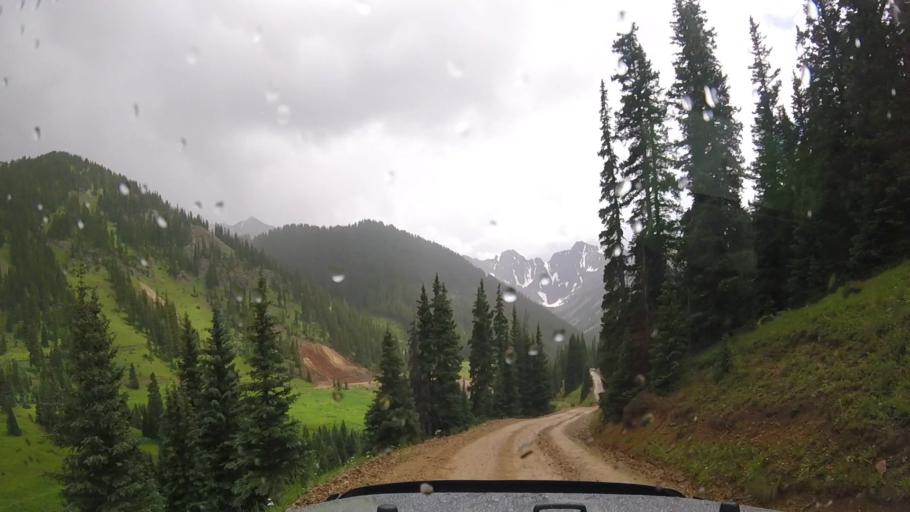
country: US
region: Colorado
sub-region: San Juan County
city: Silverton
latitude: 37.9001
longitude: -107.6470
